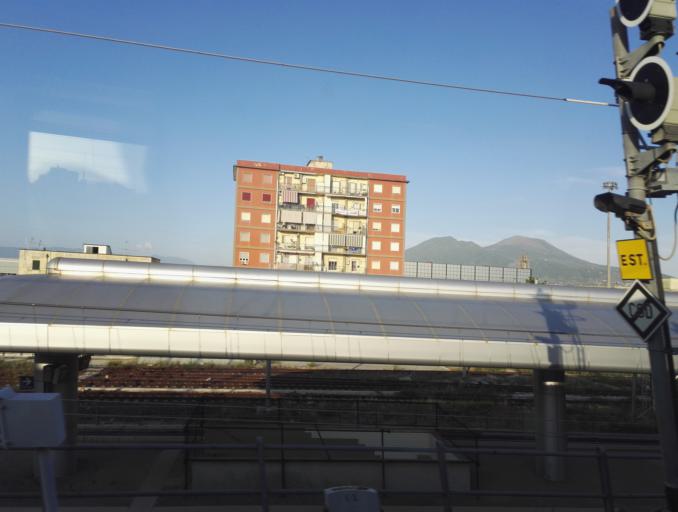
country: IT
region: Campania
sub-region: Provincia di Napoli
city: Arpino
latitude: 40.8585
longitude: 14.2972
